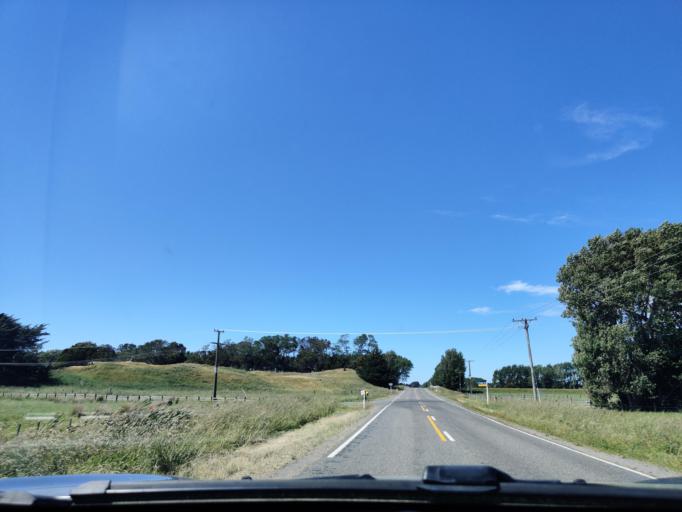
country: NZ
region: Wellington
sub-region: Upper Hutt City
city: Upper Hutt
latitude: -41.2643
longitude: 175.2779
